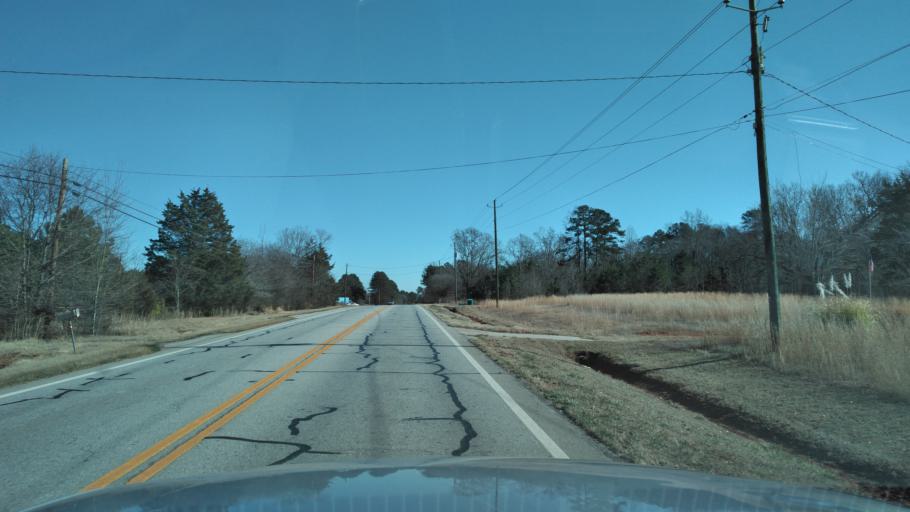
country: US
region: Georgia
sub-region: Banks County
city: Maysville
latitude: 34.2372
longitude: -83.5103
